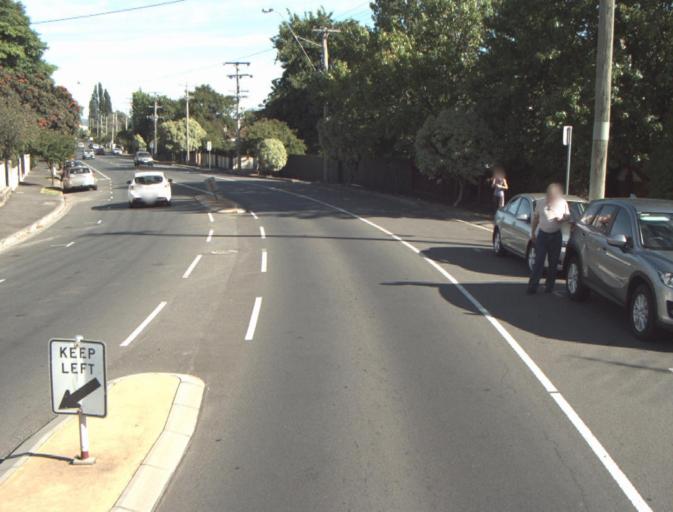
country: AU
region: Tasmania
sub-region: Launceston
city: East Launceston
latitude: -41.4361
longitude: 147.1568
